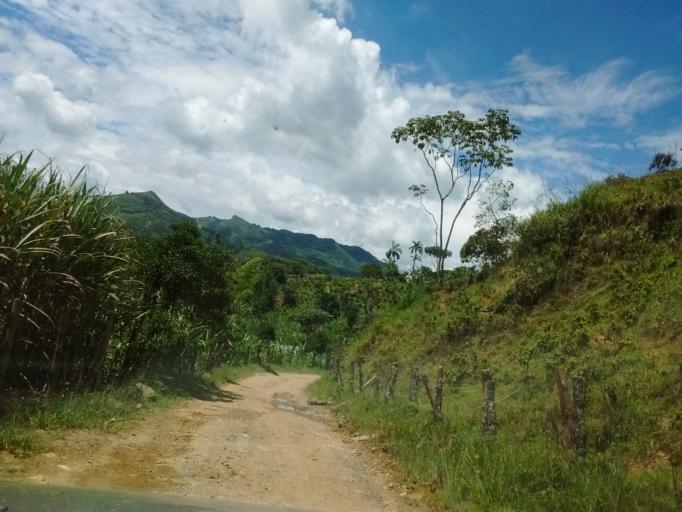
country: CO
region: Cauca
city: Villa Rica
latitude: 2.6449
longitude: -76.7711
